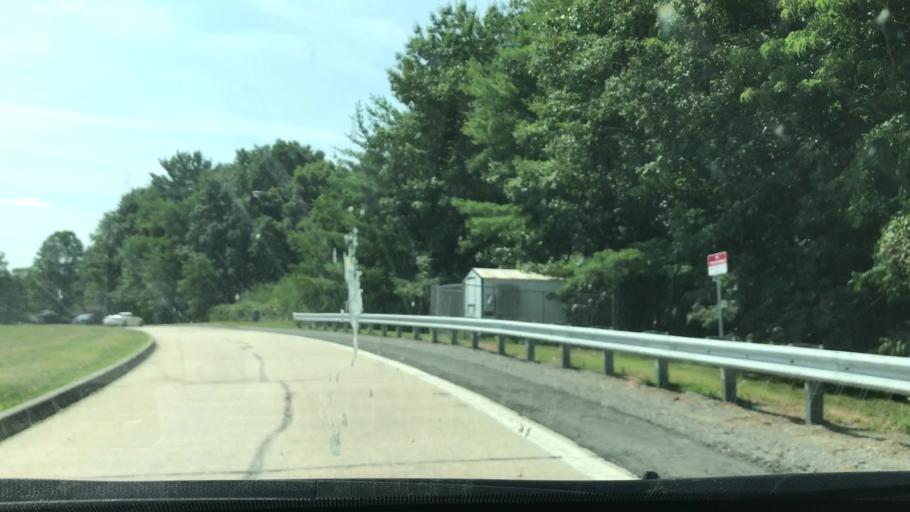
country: US
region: West Virginia
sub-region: Mercer County
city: Athens
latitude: 37.4867
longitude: -81.0815
